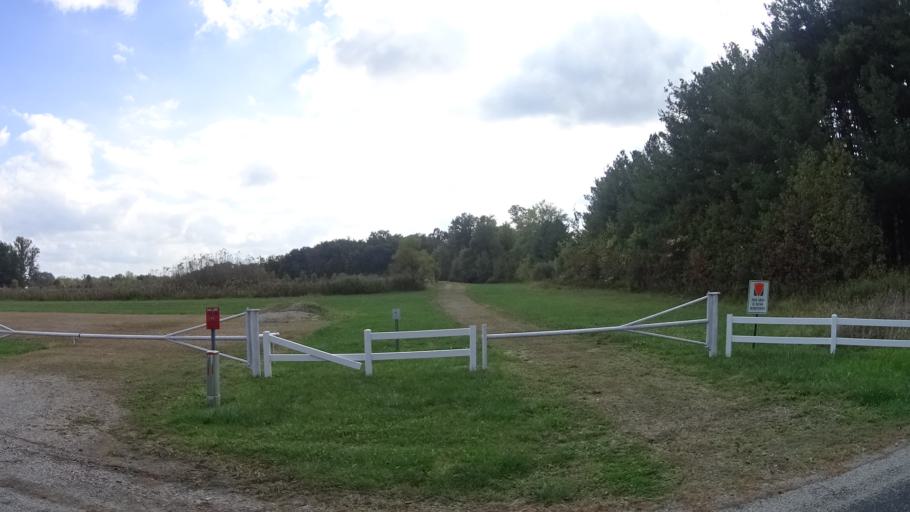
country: US
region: Ohio
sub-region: Lorain County
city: Grafton
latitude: 41.2642
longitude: -82.0731
